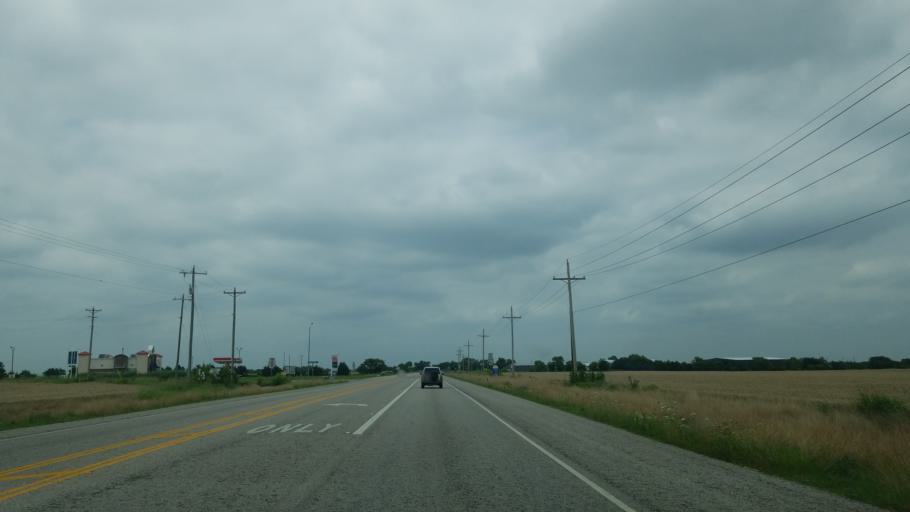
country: US
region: Texas
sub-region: Denton County
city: Pilot Point
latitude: 33.4115
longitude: -96.9411
